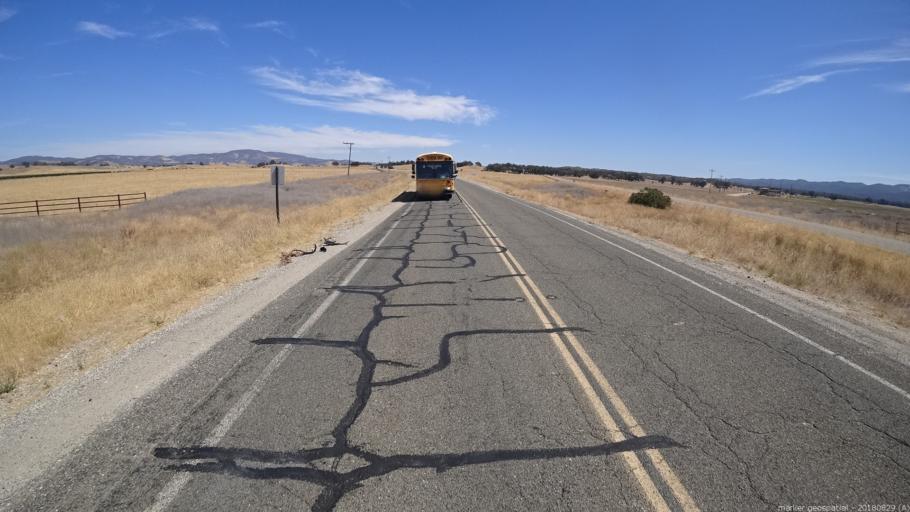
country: US
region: California
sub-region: Monterey County
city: King City
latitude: 35.9426
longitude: -121.1323
